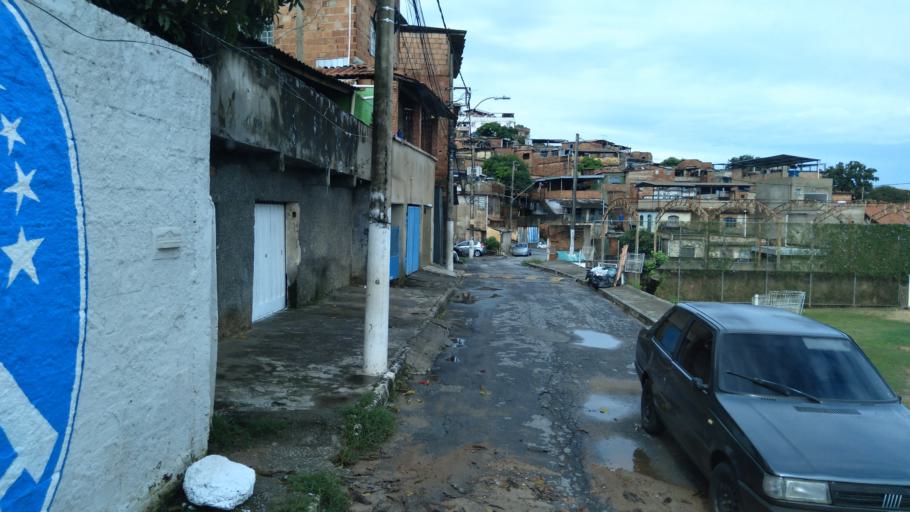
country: BR
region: Minas Gerais
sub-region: Belo Horizonte
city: Belo Horizonte
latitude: -19.9049
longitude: -43.8907
